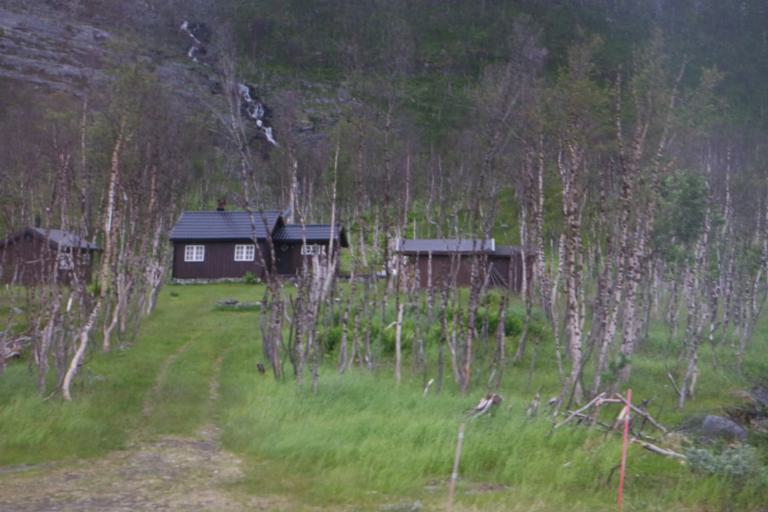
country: NO
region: Finnmark Fylke
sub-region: Kvalsund
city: Kvalsund
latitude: 70.3218
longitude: 24.2414
